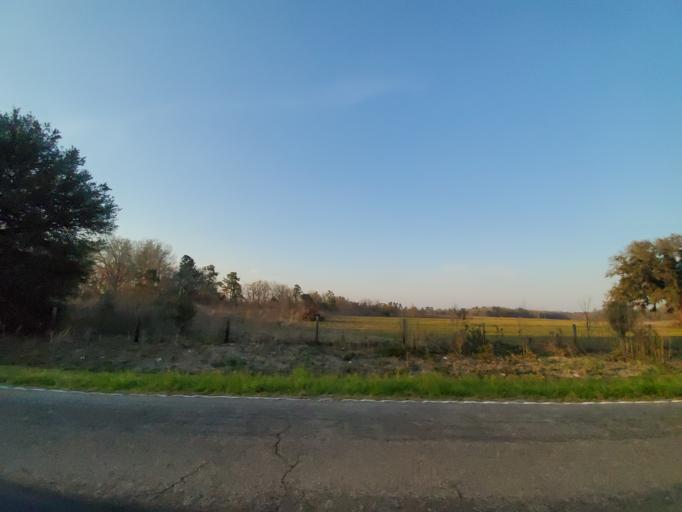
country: US
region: South Carolina
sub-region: Dorchester County
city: Saint George
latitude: 33.0456
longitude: -80.5846
